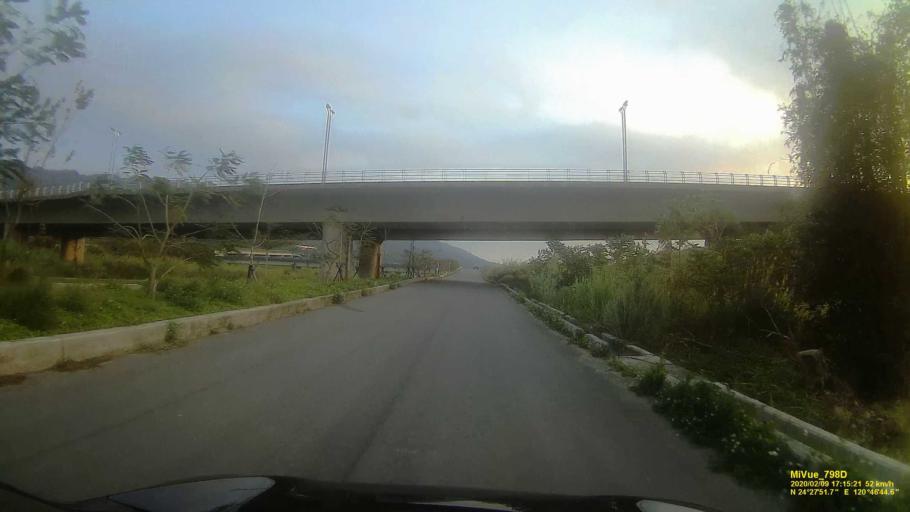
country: TW
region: Taiwan
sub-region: Miaoli
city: Miaoli
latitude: 24.4642
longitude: 120.7791
